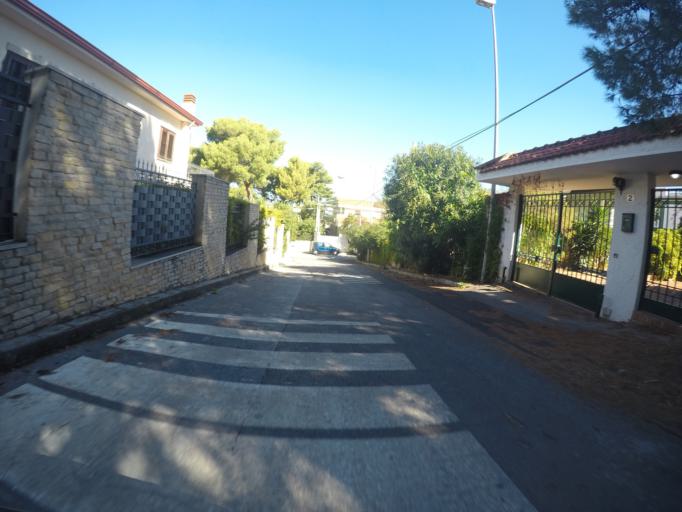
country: IT
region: Sicily
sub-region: Palermo
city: Palermo
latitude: 38.1875
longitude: 13.3479
